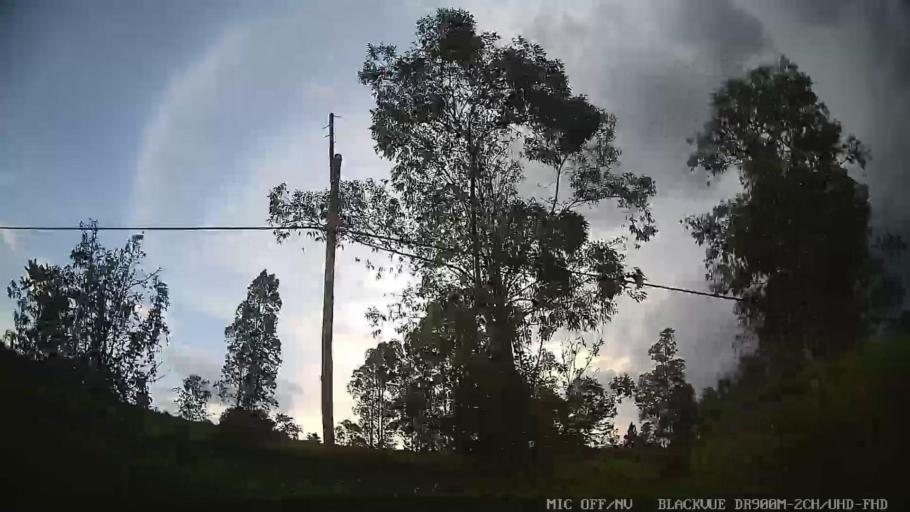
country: BR
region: Sao Paulo
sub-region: Itatiba
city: Itatiba
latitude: -22.9885
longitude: -46.8450
